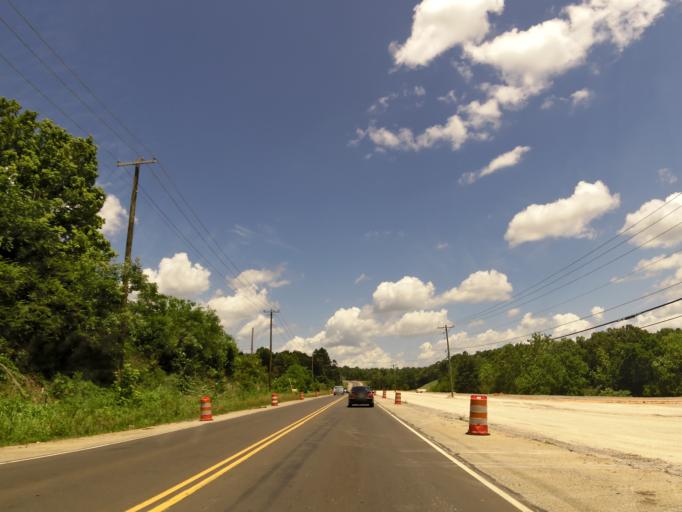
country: US
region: Tennessee
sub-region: Union County
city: Condon
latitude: 36.1275
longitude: -83.9147
